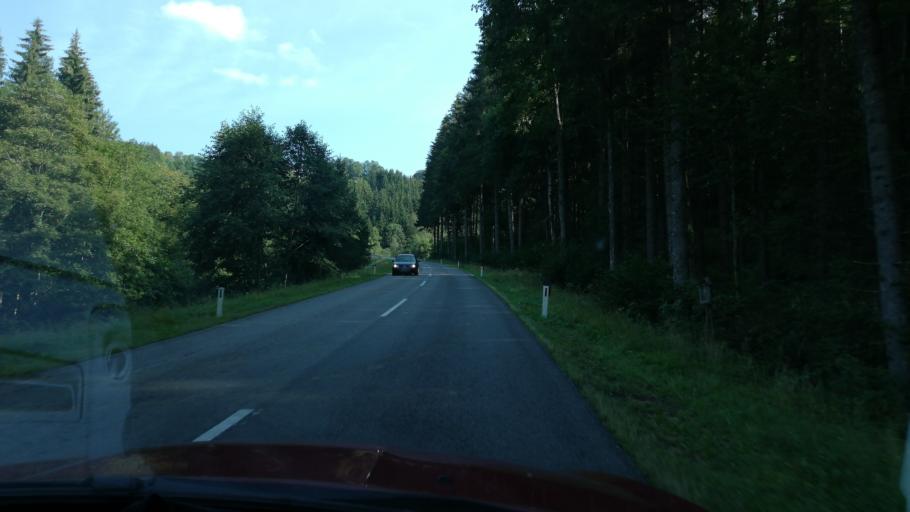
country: AT
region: Lower Austria
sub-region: Politischer Bezirk Zwettl
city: Langschlag
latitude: 48.4609
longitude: 14.7961
